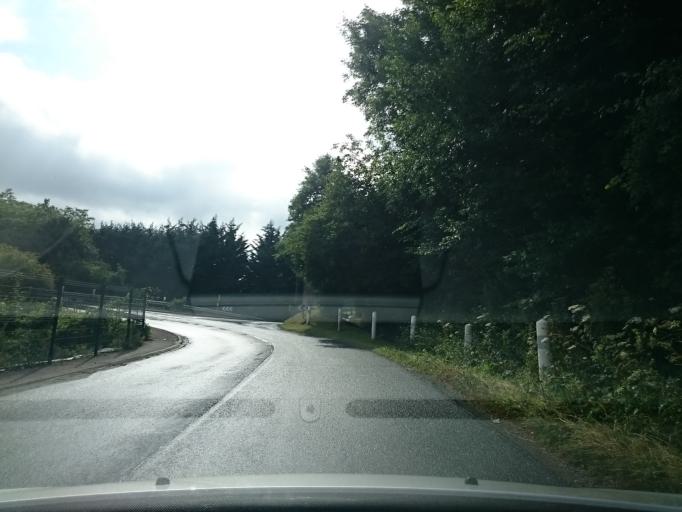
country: FR
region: Lower Normandy
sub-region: Departement du Calvados
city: Beuvillers
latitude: 49.1281
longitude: 0.2533
